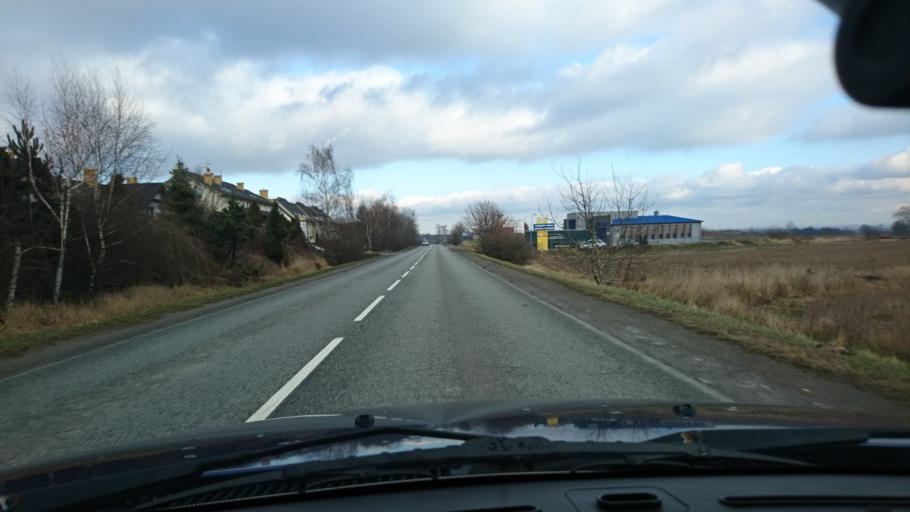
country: PL
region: Silesian Voivodeship
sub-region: Powiat mikolowski
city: Mikolow
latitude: 50.1565
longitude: 18.9038
